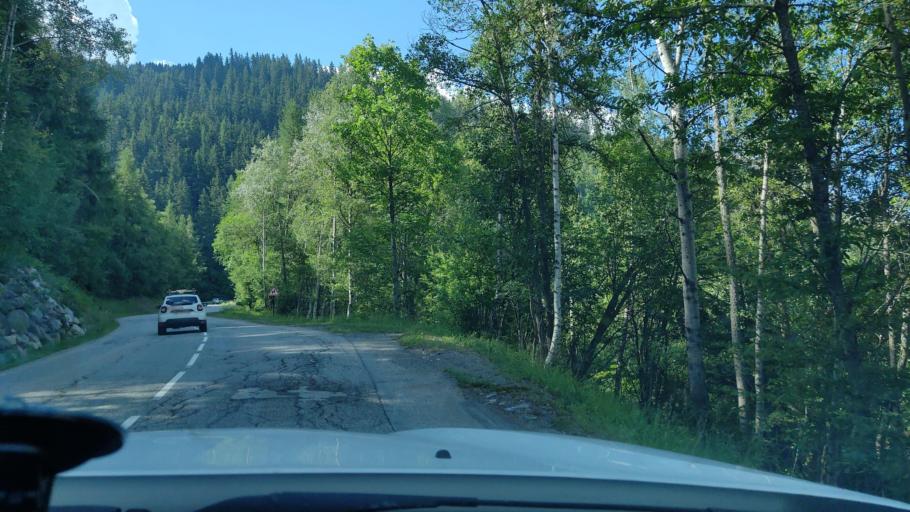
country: FR
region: Rhone-Alpes
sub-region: Departement de la Savoie
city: Bourg-Saint-Maurice
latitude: 45.5867
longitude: 6.7804
